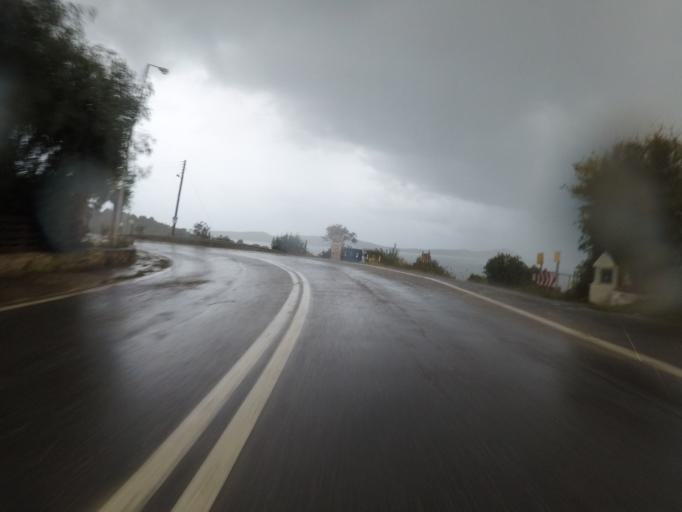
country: GR
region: Peloponnese
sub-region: Nomos Messinias
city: Pylos
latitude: 36.9257
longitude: 21.7136
